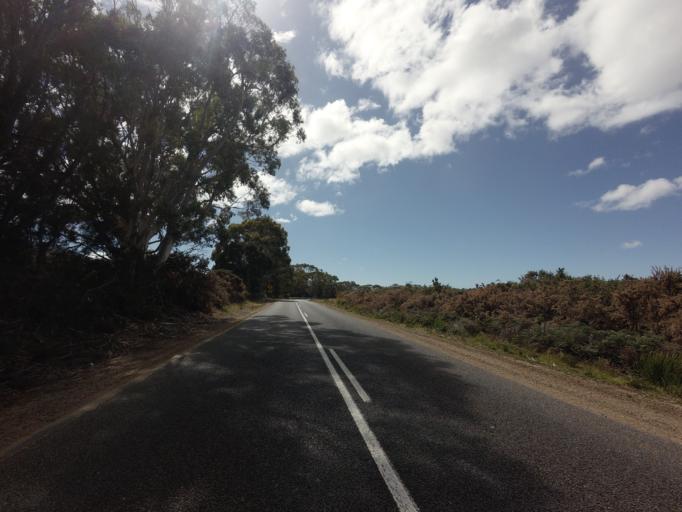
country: AU
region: Tasmania
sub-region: Break O'Day
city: St Helens
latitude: -41.9288
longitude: 148.2289
